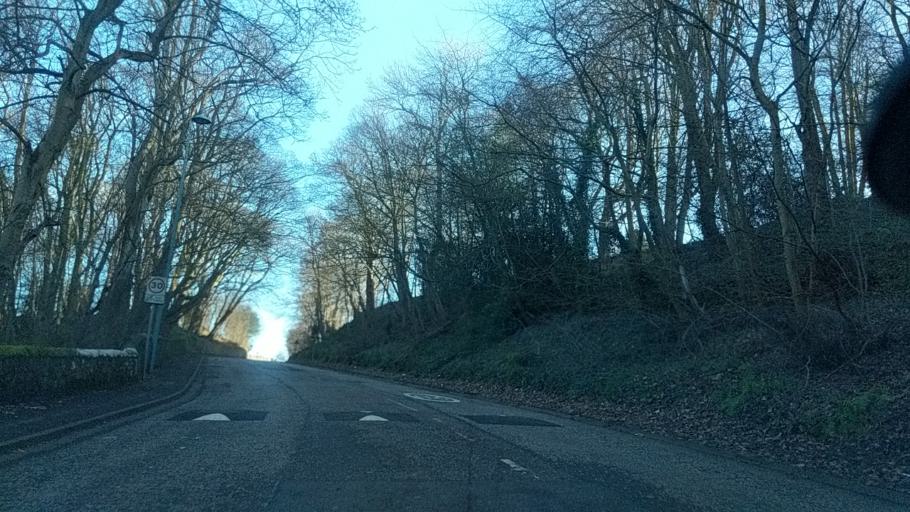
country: GB
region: Scotland
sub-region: Edinburgh
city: Queensferry
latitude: 55.9900
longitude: -3.3824
